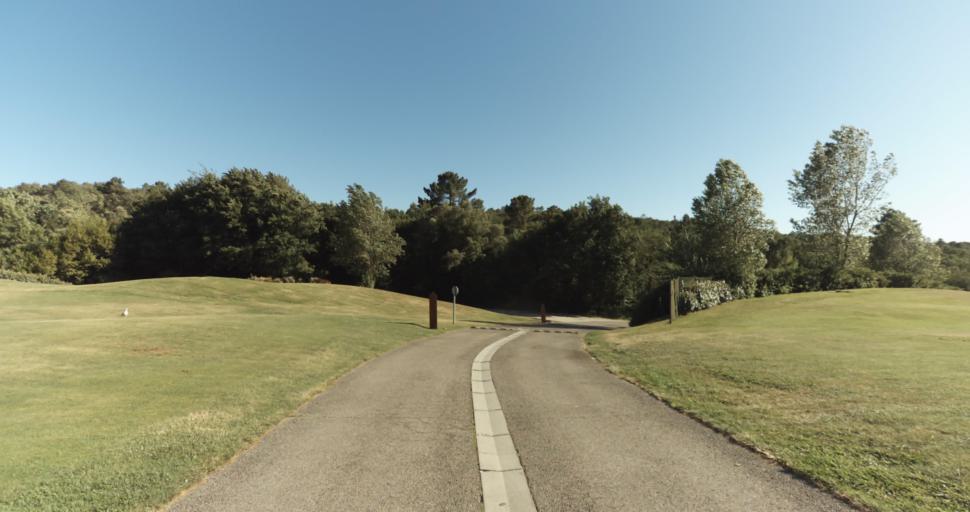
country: FR
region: Provence-Alpes-Cote d'Azur
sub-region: Departement du Var
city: Gassin
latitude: 43.2522
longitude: 6.6061
